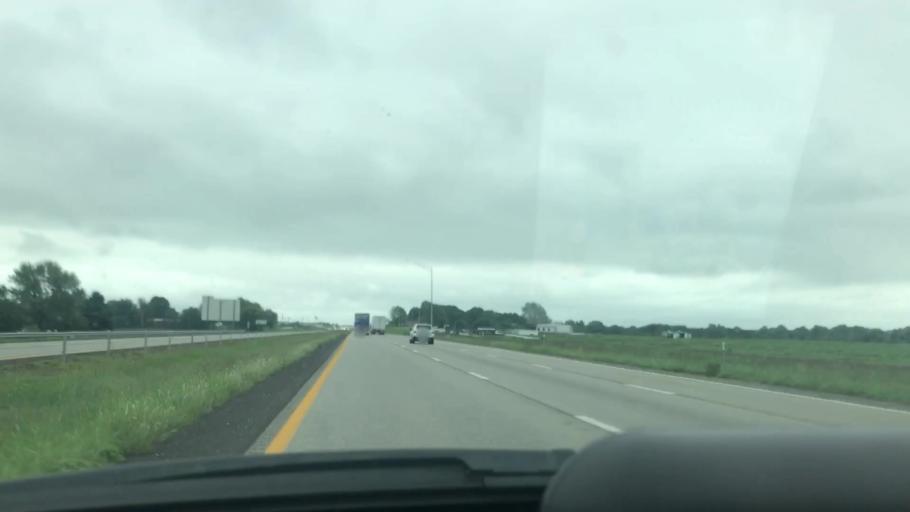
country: US
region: Missouri
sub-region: Greene County
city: Republic
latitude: 37.1971
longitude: -93.4394
